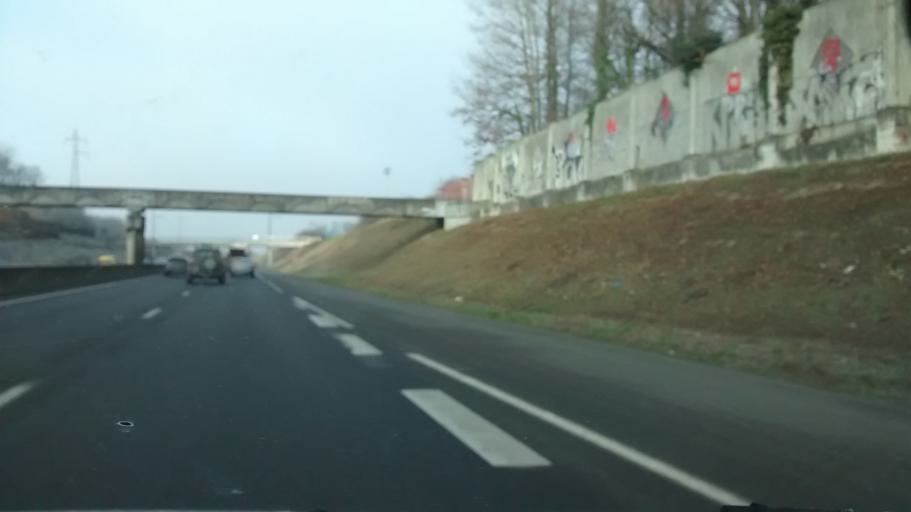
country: FR
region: Centre
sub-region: Departement d'Indre-et-Loire
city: Joue-les-Tours
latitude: 47.3408
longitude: 0.6631
